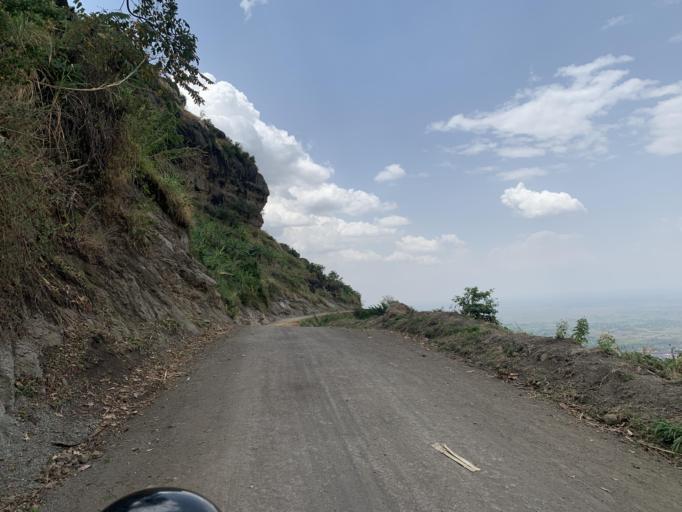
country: UG
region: Eastern Region
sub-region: Sironko District
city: Sironko
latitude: 1.2623
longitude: 34.3002
